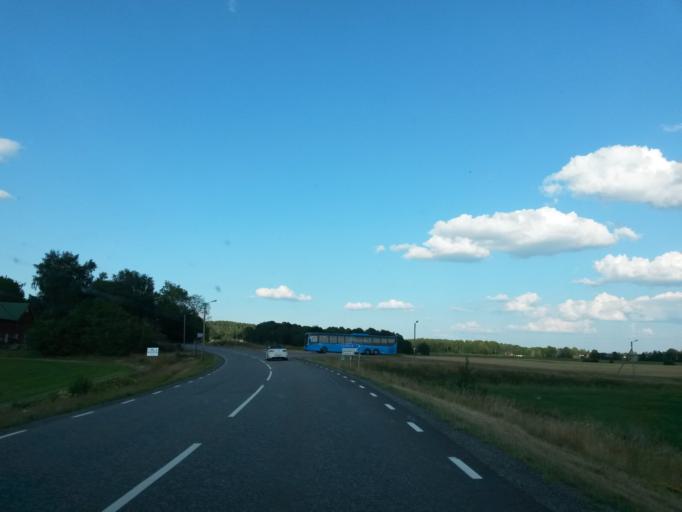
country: SE
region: Vaestra Goetaland
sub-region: Lerums Kommun
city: Grabo
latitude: 57.9187
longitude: 12.3495
